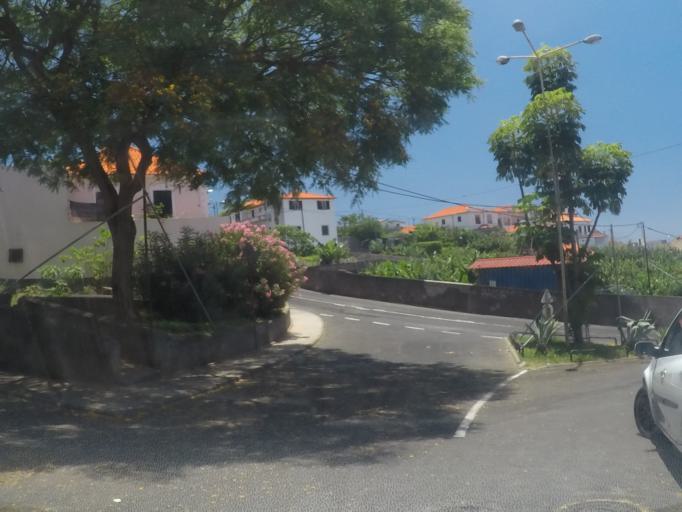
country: PT
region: Madeira
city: Camara de Lobos
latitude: 32.6514
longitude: -16.9701
